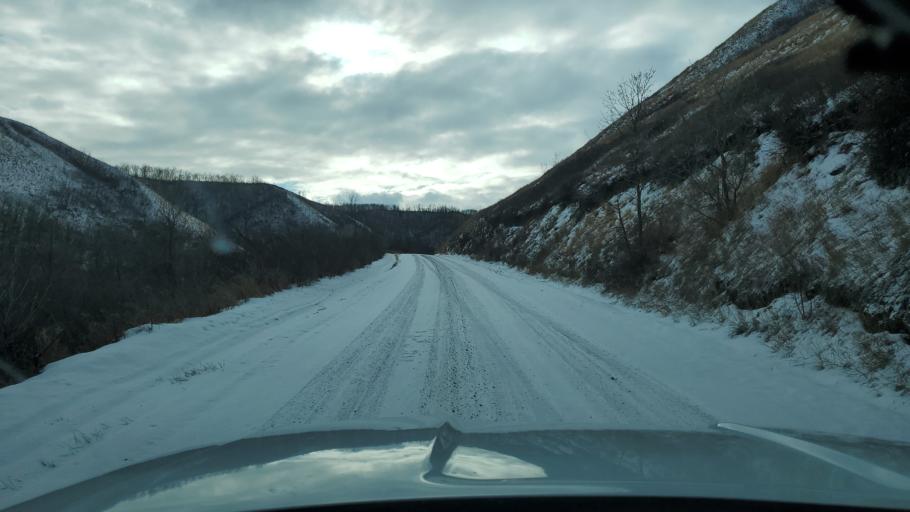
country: CA
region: Saskatchewan
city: White City
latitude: 50.7755
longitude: -104.1415
